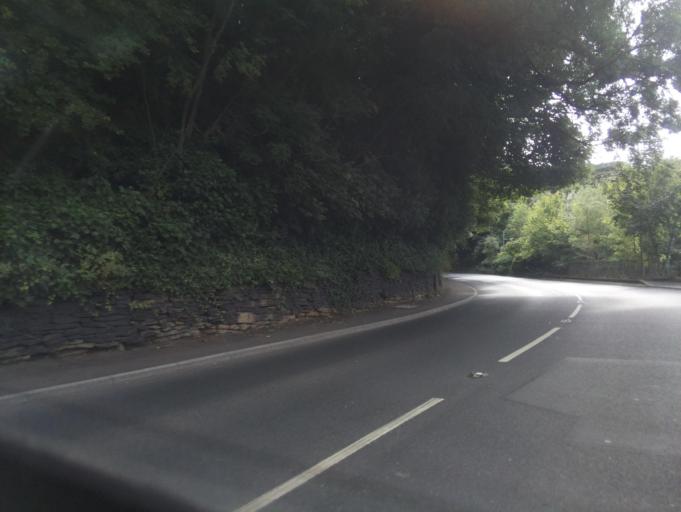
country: GB
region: England
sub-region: Kirklees
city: Holmfirth
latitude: 53.5749
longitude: -1.7539
